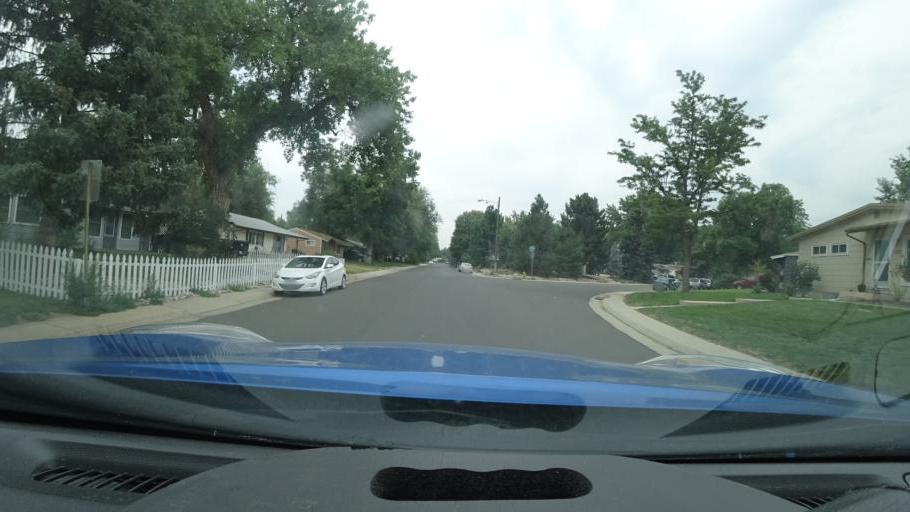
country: US
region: Colorado
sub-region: Arapahoe County
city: Glendale
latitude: 39.6923
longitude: -104.9174
